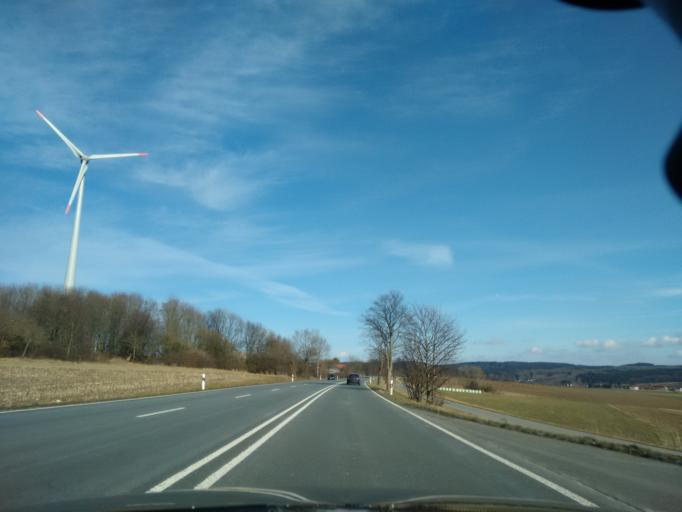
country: DE
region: North Rhine-Westphalia
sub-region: Regierungsbezirk Detmold
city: Altenbeken
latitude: 51.7357
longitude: 8.9259
